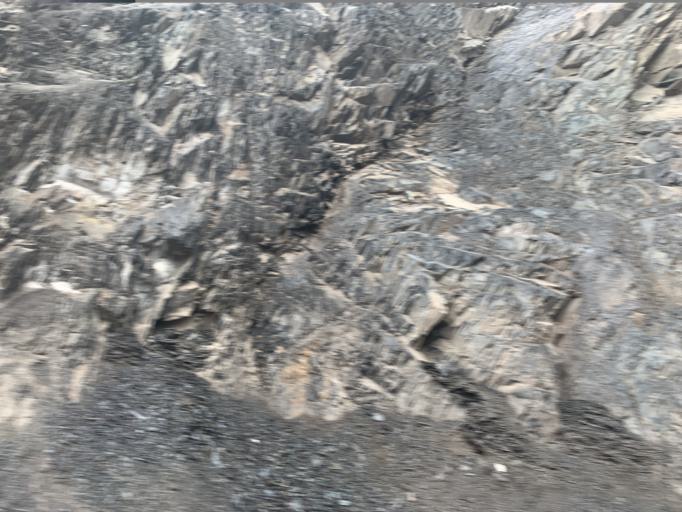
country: IR
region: Mazandaran
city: Amol
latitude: 36.1135
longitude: 52.2817
